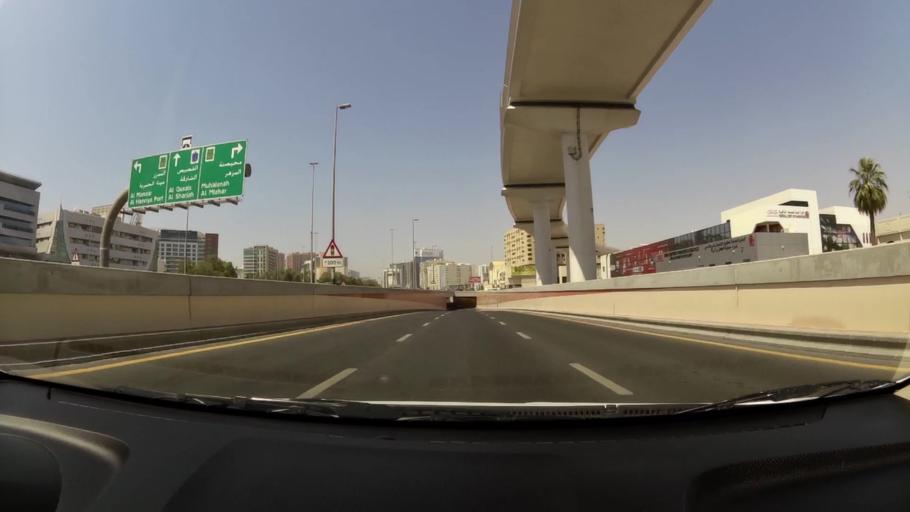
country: AE
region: Ash Shariqah
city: Sharjah
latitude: 25.2793
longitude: 55.3544
